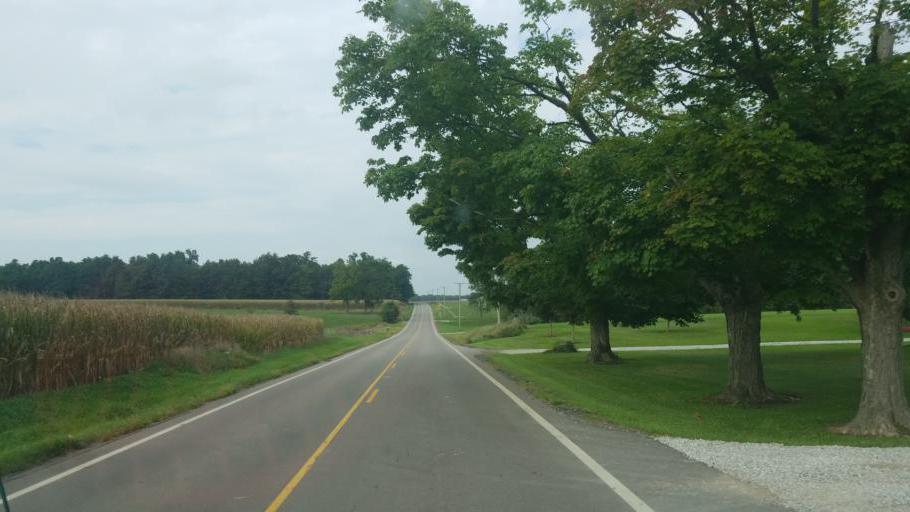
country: US
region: Ohio
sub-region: Wayne County
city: West Salem
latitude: 40.9038
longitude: -82.0519
